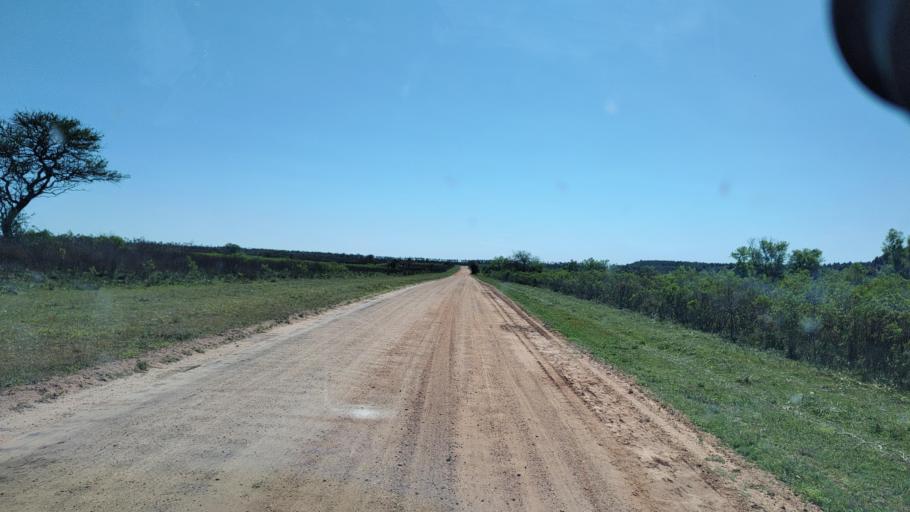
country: AR
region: Entre Rios
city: Ubajay
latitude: -31.8643
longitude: -58.2623
